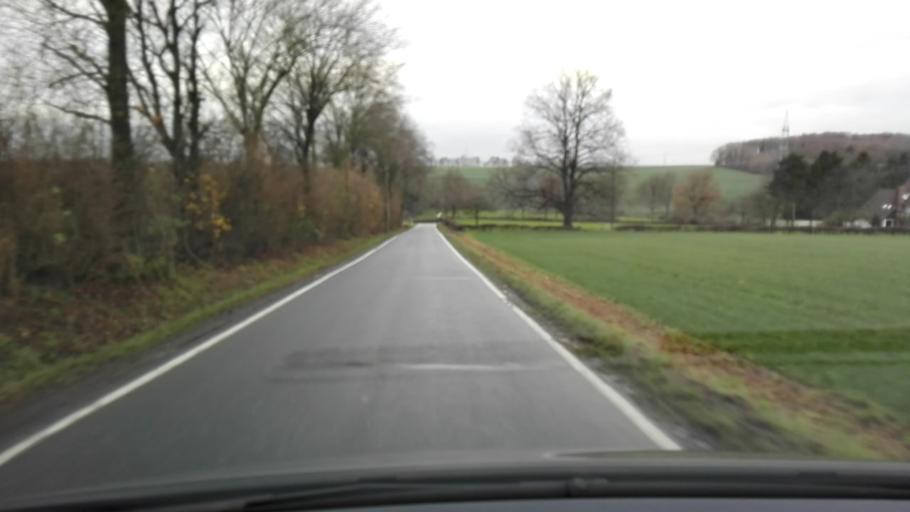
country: DE
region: North Rhine-Westphalia
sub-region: Regierungsbezirk Arnsberg
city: Frondenberg
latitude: 51.5154
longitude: 7.7496
